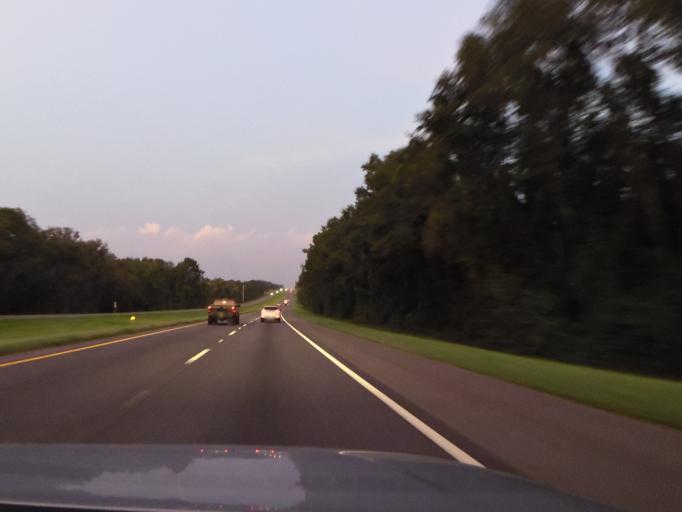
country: US
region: Florida
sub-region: Madison County
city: Madison
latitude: 30.4360
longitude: -83.5160
